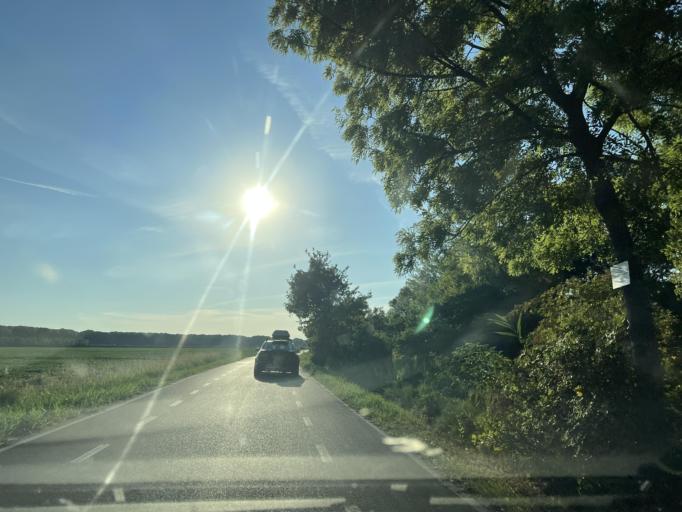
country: IT
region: Friuli Venezia Giulia
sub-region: Provincia di Gorizia
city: San Canzian d'Isonzo
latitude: 45.7742
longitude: 13.4828
